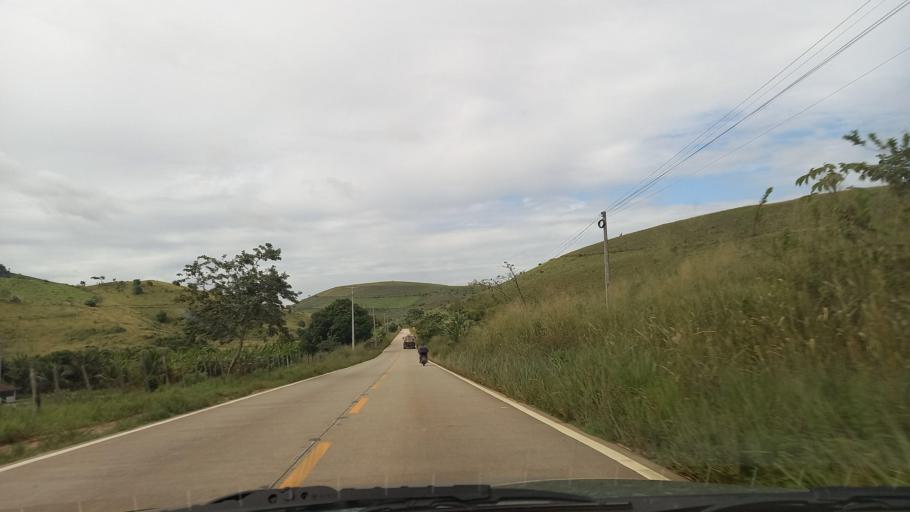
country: BR
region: Pernambuco
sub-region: Maraial
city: Maraial
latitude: -8.7542
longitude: -35.8406
